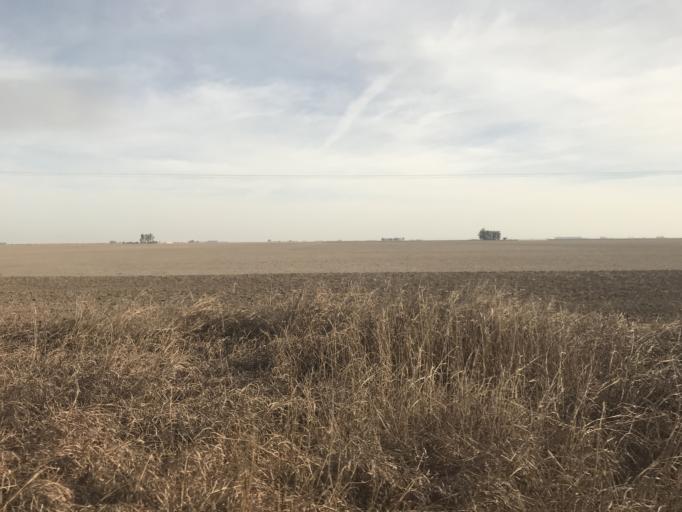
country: AR
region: Cordoba
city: Laguna Larga
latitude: -31.7343
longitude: -63.8402
